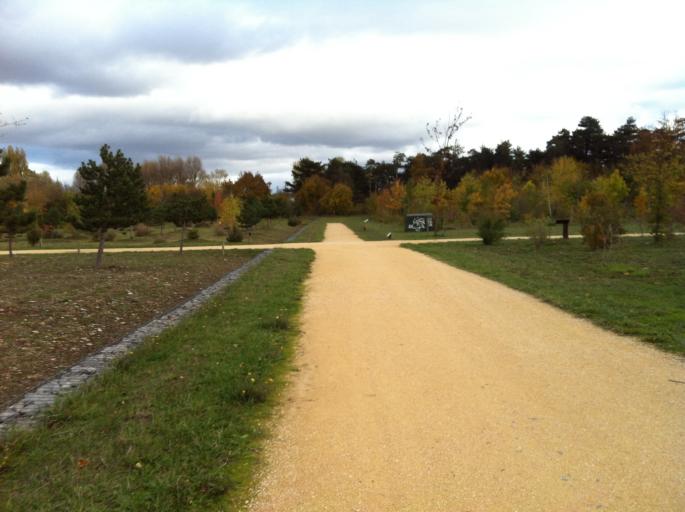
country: ES
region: Basque Country
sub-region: Provincia de Alava
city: Gasteiz / Vitoria
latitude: 42.8300
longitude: -2.6630
